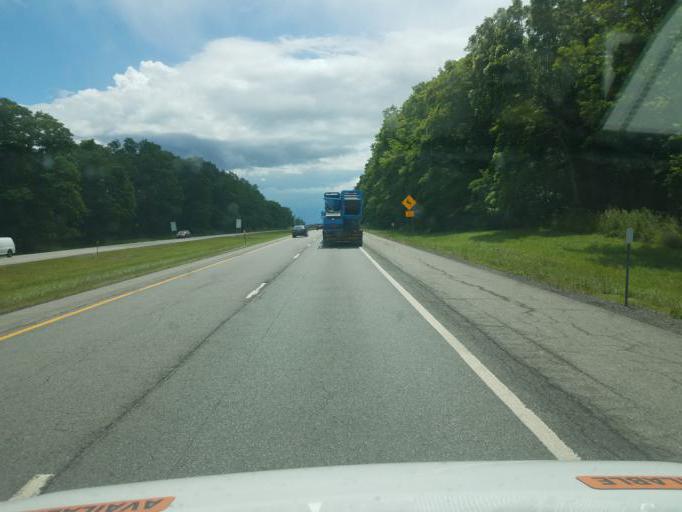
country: US
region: New York
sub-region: Monroe County
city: Pittsford
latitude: 43.0272
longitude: -77.5071
